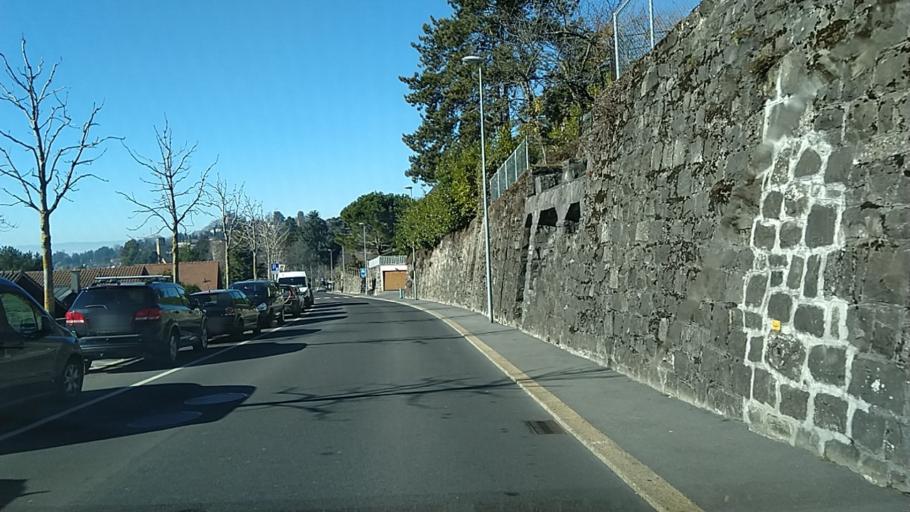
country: CH
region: Vaud
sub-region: Riviera-Pays-d'Enhaut District
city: Le Chatelard
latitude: 46.4419
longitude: 6.9036
